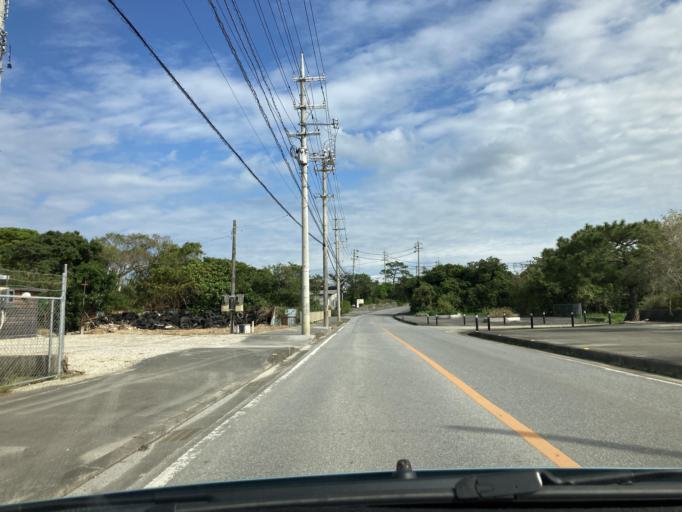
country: JP
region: Okinawa
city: Nago
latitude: 26.6911
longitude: 127.9607
